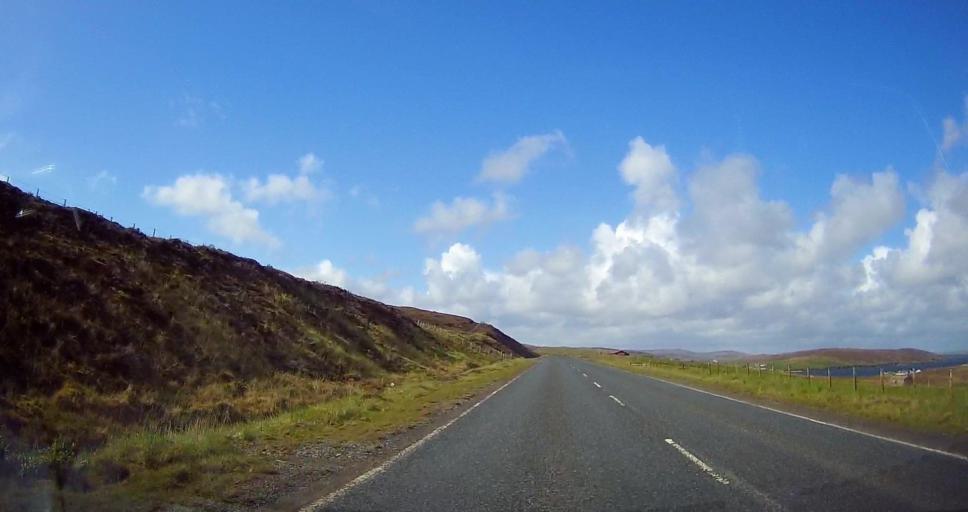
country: GB
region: Scotland
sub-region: Shetland Islands
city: Lerwick
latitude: 60.2193
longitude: -1.2342
